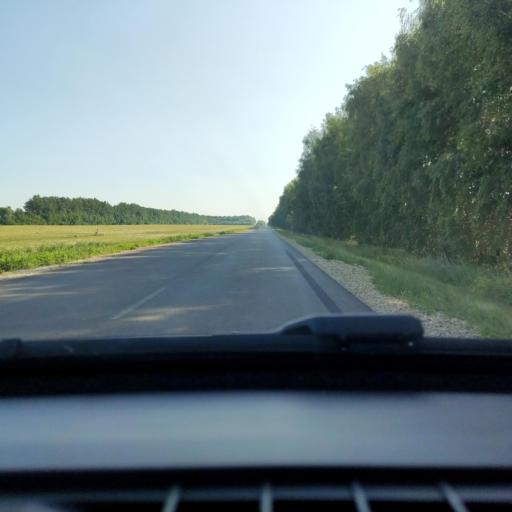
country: RU
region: Voronezj
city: Pereleshinskiy
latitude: 51.6415
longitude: 40.2877
